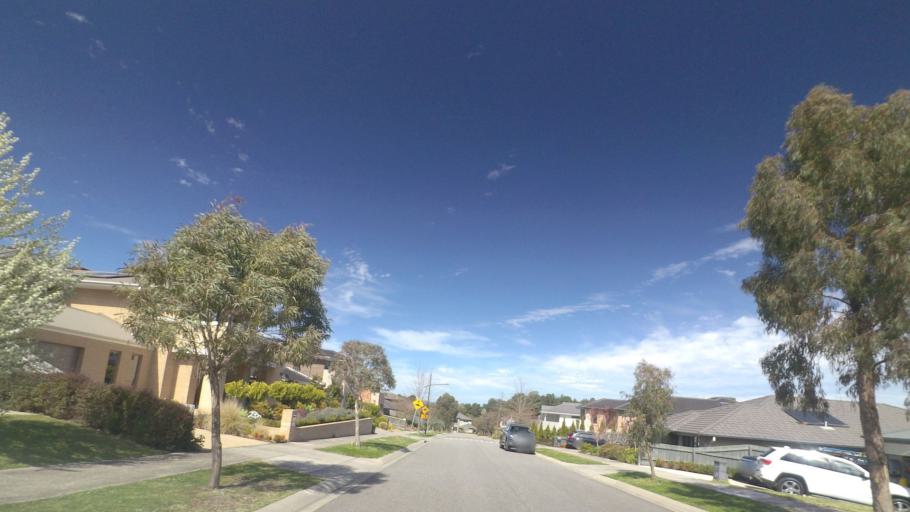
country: AU
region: Victoria
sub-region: Maroondah
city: Croydon South
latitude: -37.8155
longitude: 145.2643
